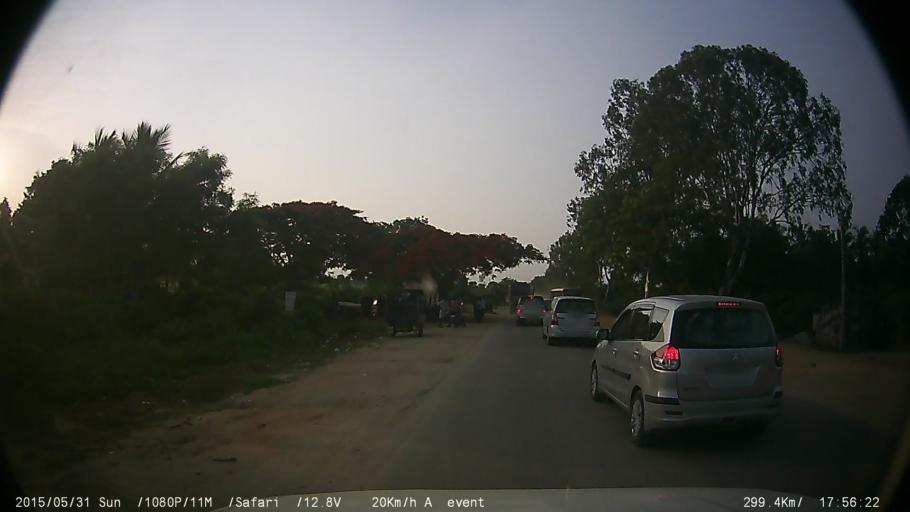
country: IN
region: Karnataka
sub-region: Mysore
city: Nanjangud
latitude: 11.9953
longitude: 76.6696
